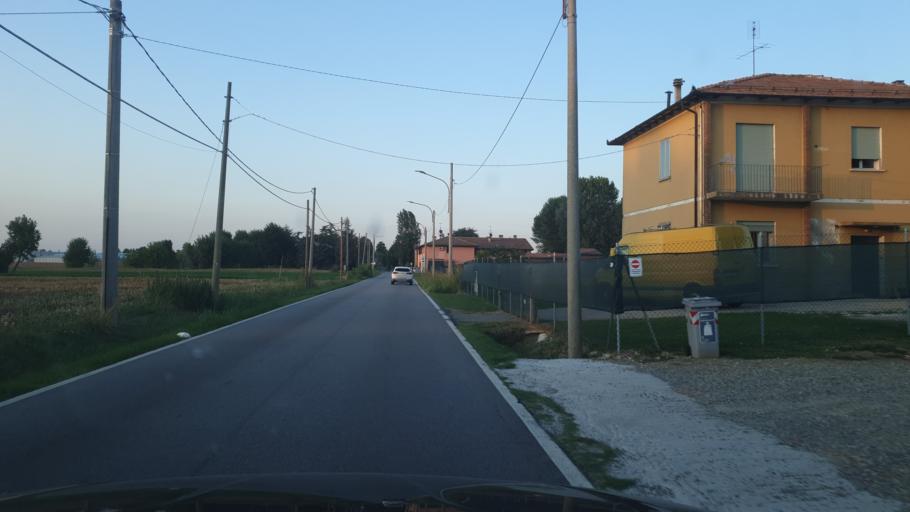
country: IT
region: Emilia-Romagna
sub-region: Provincia di Bologna
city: Quarto Inferiore
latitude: 44.5377
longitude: 11.3923
